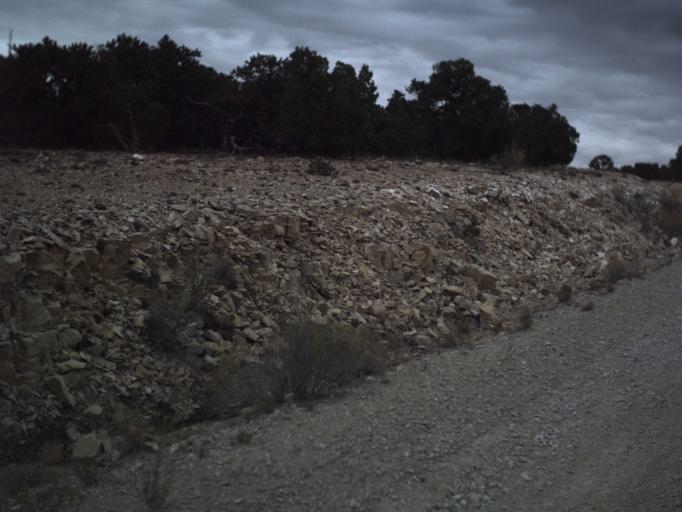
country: US
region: Utah
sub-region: Emery County
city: Ferron
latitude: 38.8523
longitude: -110.9098
